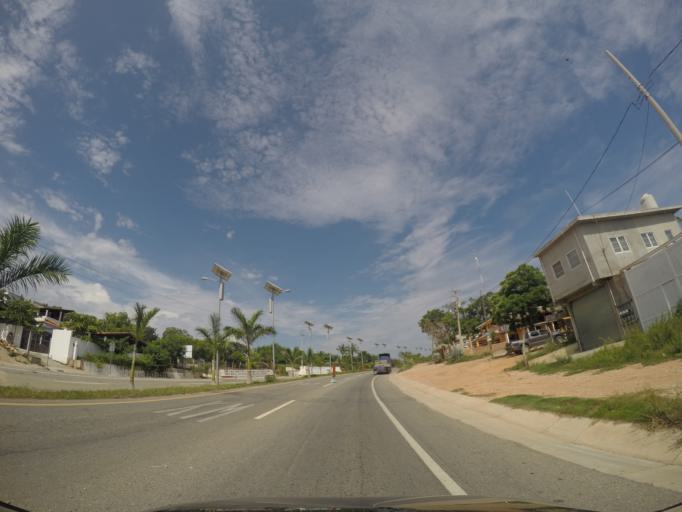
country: MX
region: Oaxaca
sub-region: Santa Maria Colotepec
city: Brisas de Zicatela
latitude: 15.8275
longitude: -97.0244
